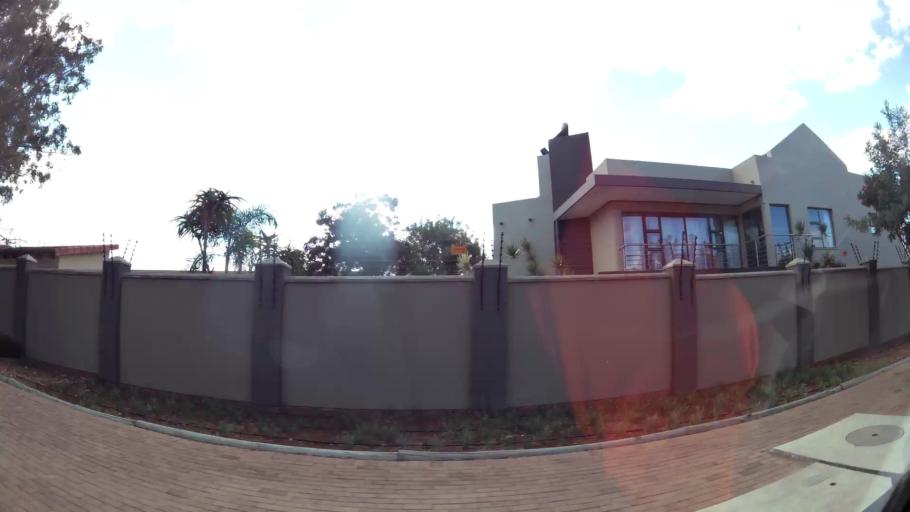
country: ZA
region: Limpopo
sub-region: Capricorn District Municipality
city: Polokwane
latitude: -23.8945
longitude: 29.4771
